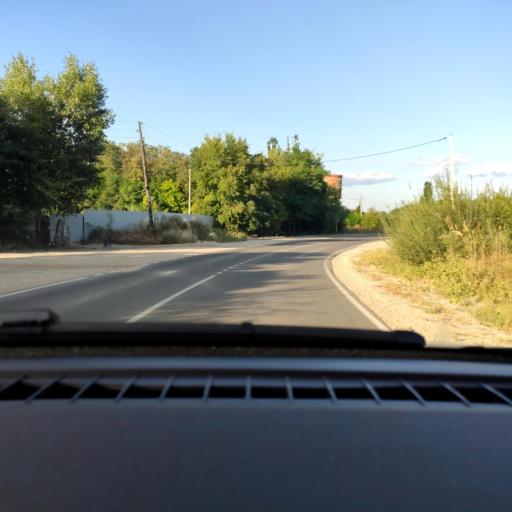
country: RU
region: Voronezj
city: Semiluki
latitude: 51.6639
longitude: 39.0120
